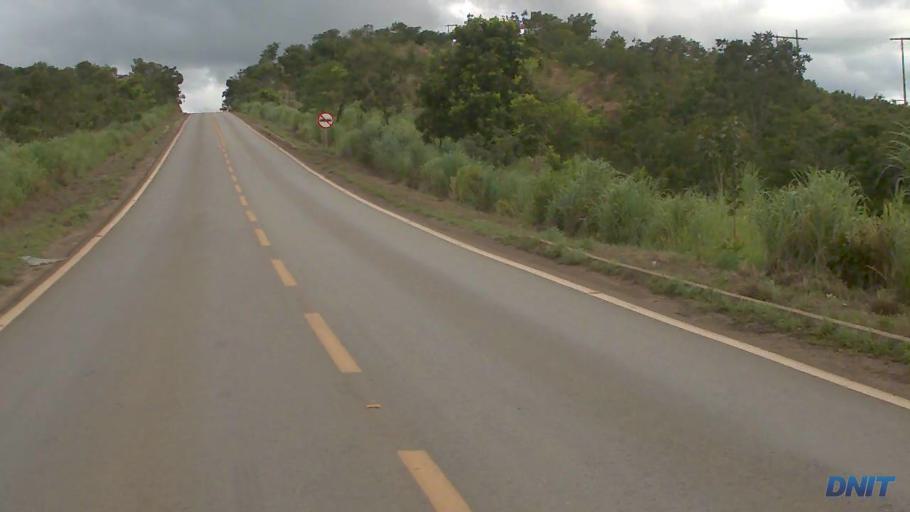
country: BR
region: Goias
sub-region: Padre Bernardo
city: Padre Bernardo
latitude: -15.2136
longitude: -48.2813
